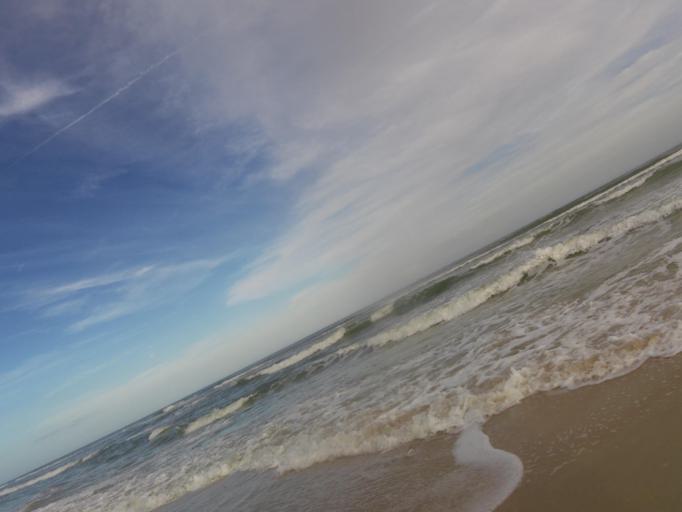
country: US
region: Florida
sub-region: Flagler County
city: Palm Coast
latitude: 29.6064
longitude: -81.1857
